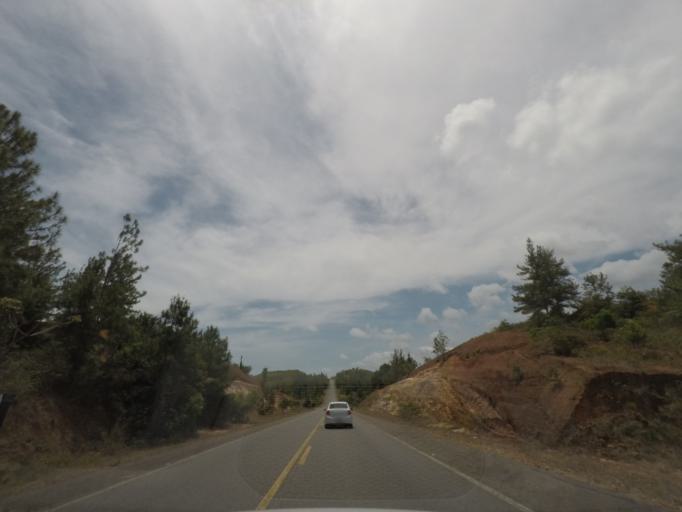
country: BR
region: Bahia
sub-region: Conde
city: Conde
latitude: -11.9960
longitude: -37.6801
